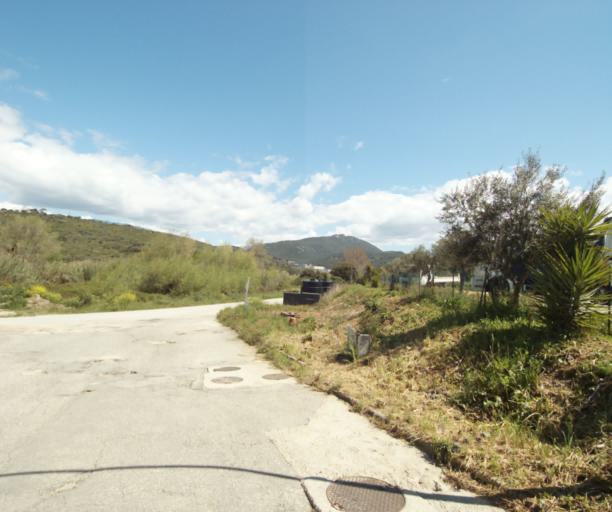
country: FR
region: Corsica
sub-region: Departement de la Corse-du-Sud
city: Propriano
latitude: 41.6573
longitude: 8.9024
